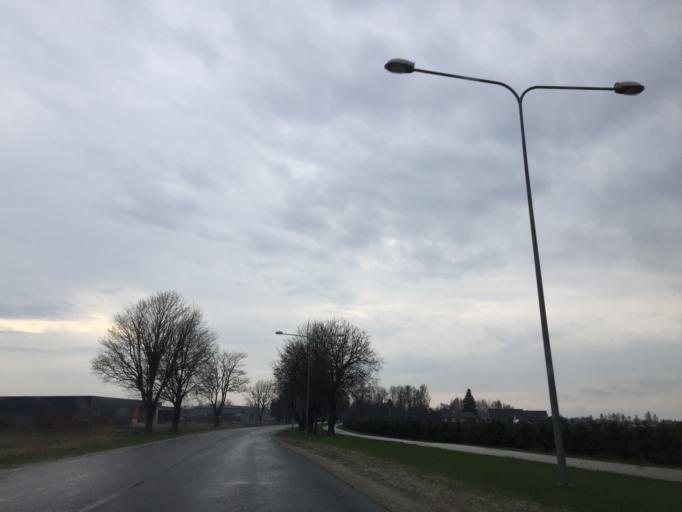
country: EE
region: Tartu
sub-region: UElenurme vald
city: Ulenurme
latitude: 58.3264
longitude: 26.7209
